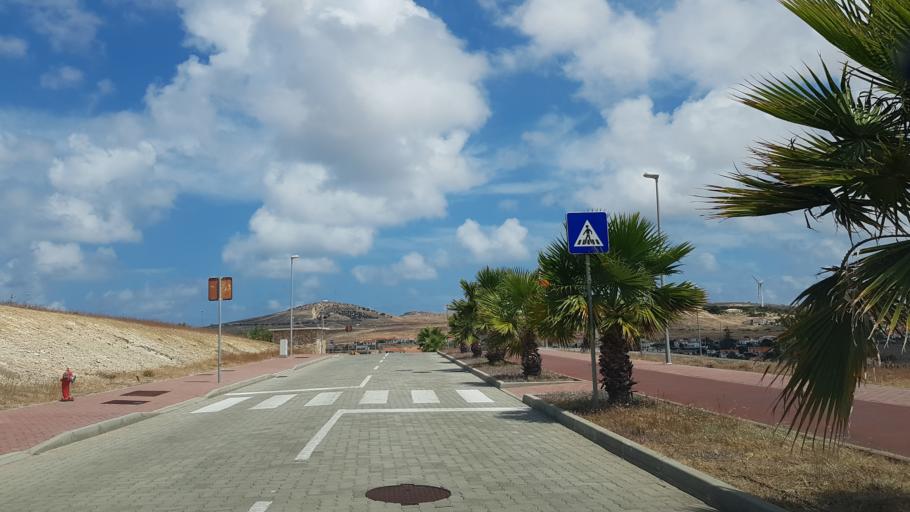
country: PT
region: Madeira
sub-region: Porto Santo
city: Vila de Porto Santo
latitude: 33.0486
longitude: -16.3644
